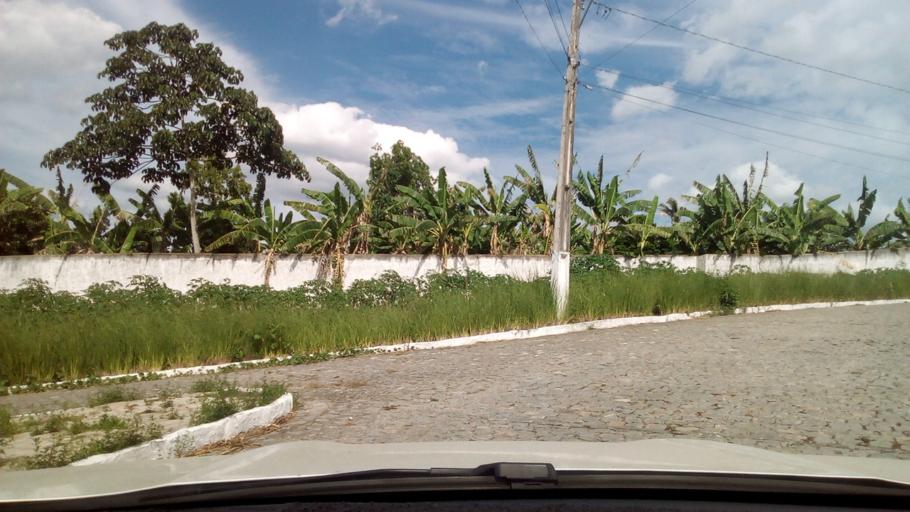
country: BR
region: Paraiba
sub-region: Guarabira
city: Guarabira
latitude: -6.8308
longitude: -35.4975
